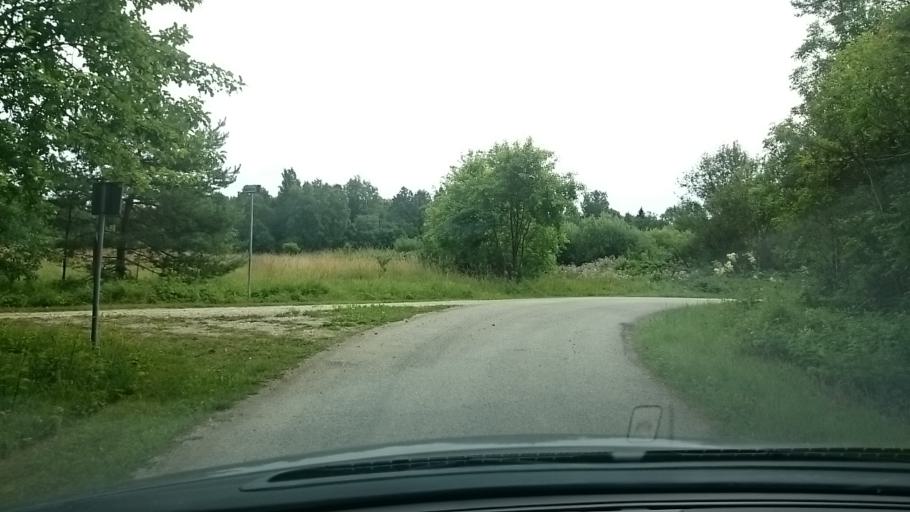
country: EE
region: Laeaene
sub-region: Ridala Parish
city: Uuemoisa
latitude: 58.9952
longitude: 23.6581
